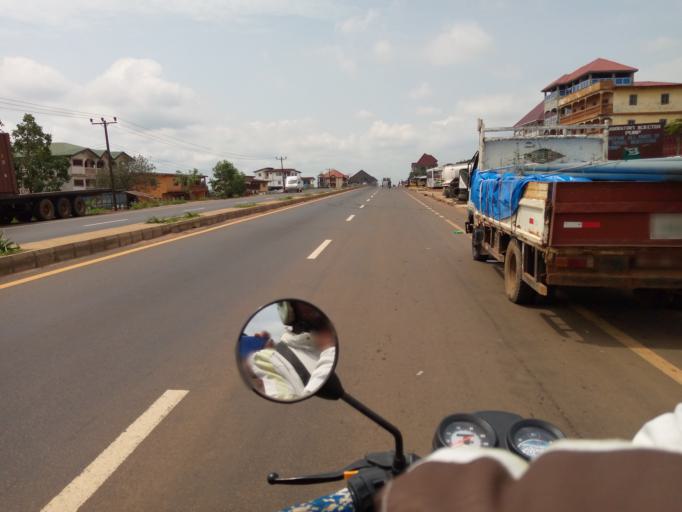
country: SL
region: Western Area
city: Waterloo
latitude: 8.3528
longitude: -13.0785
